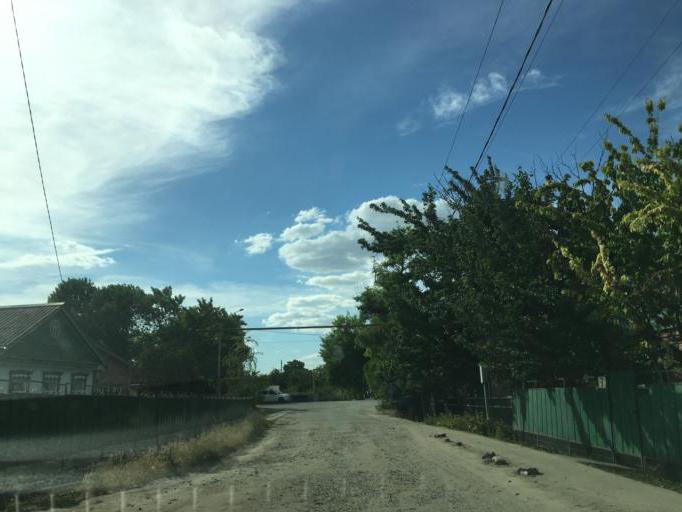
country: RU
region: Krasnodarskiy
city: Kushchevskaya
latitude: 46.5656
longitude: 39.6411
